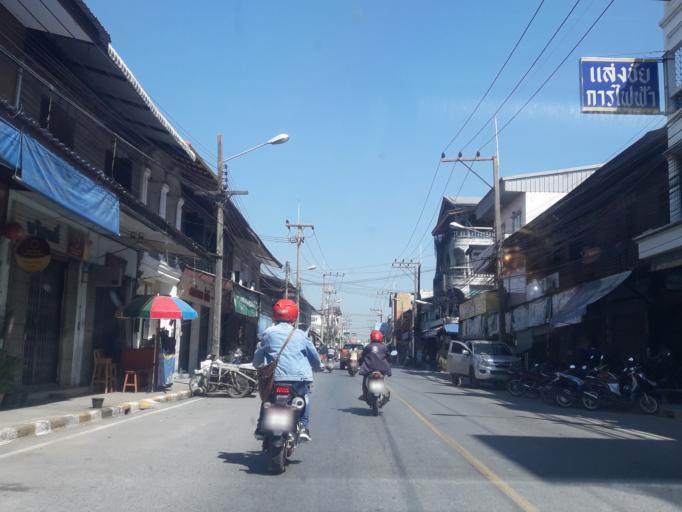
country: TH
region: Sara Buri
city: Nong Khae
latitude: 14.3377
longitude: 100.8668
